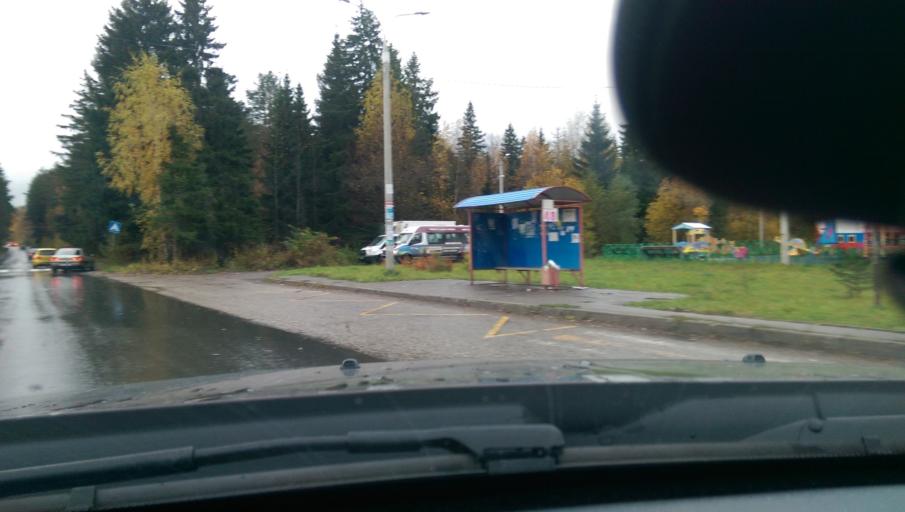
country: RU
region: Moskovskaya
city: Zelenogradskiy
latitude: 56.1289
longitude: 37.9121
